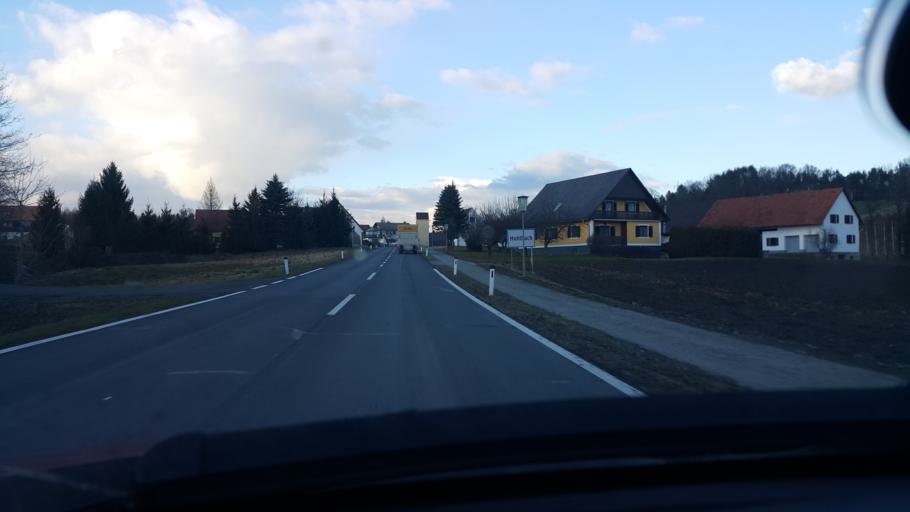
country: AT
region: Styria
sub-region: Politischer Bezirk Deutschlandsberg
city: Hollenegg
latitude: 46.7837
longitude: 15.2410
